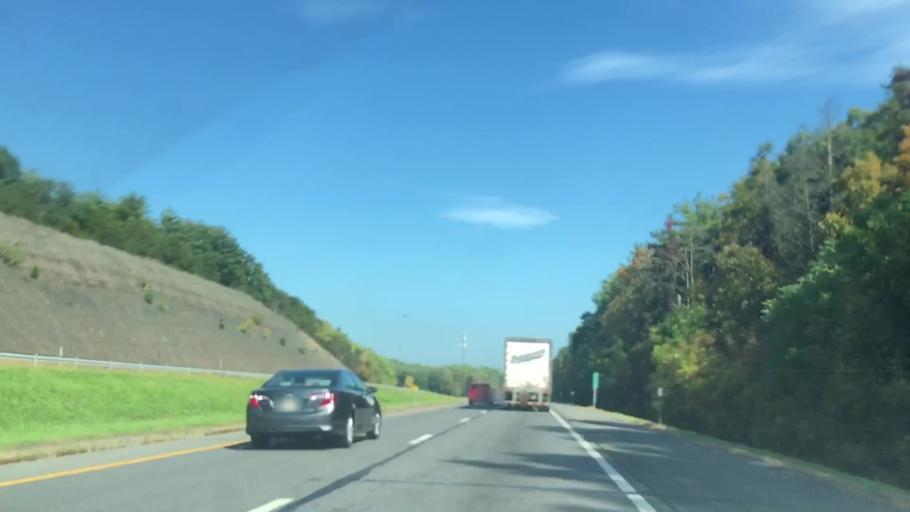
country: US
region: New York
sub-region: Greene County
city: Coxsackie
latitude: 42.3208
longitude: -73.8653
